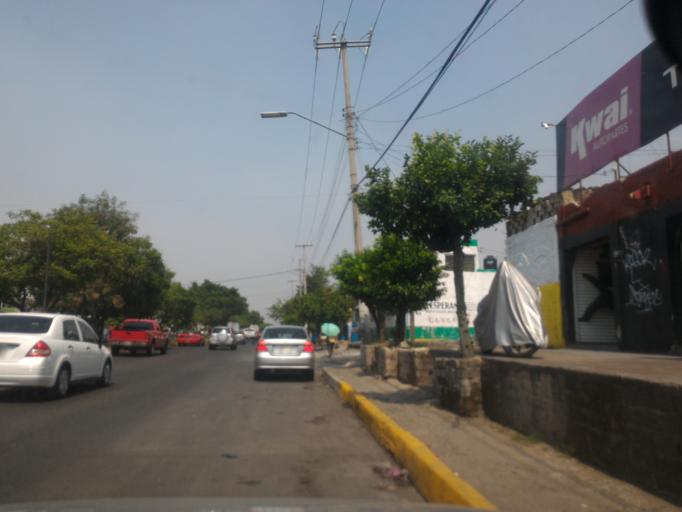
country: MX
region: Jalisco
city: Guadalajara
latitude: 20.6250
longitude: -103.3809
